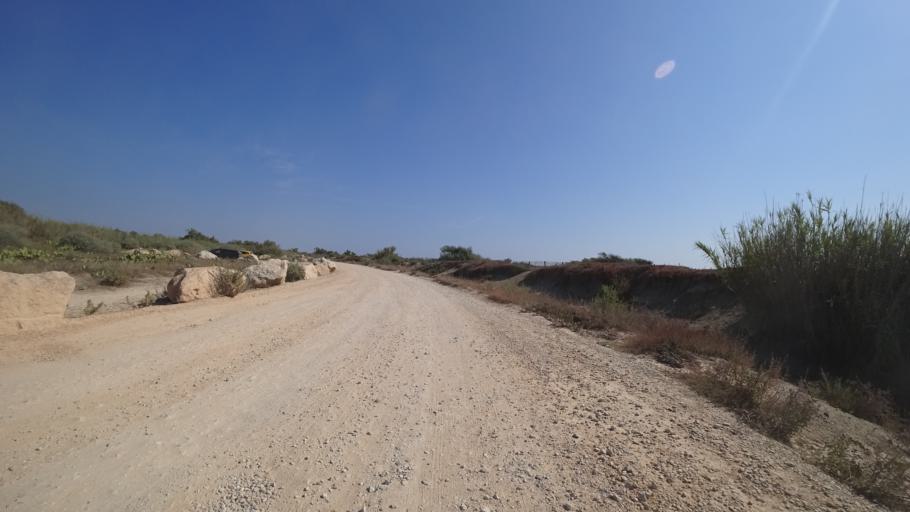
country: FR
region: Languedoc-Roussillon
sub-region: Departement des Pyrenees-Orientales
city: Le Barcares
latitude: 42.7765
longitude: 3.0371
